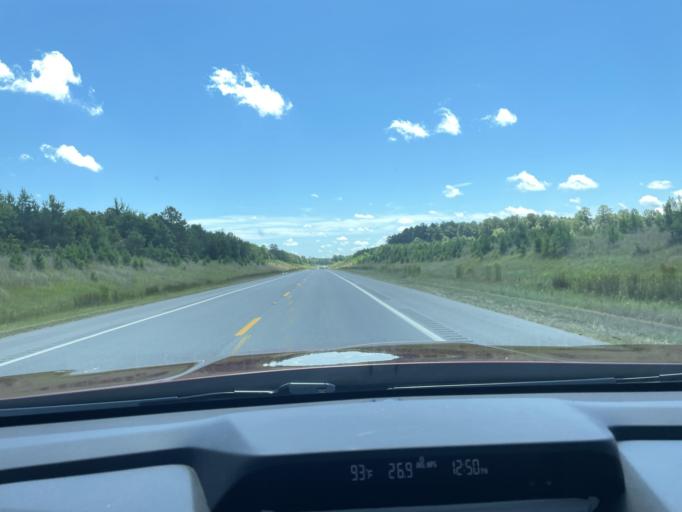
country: US
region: Arkansas
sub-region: Lincoln County
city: Star City
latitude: 33.9486
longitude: -91.9004
